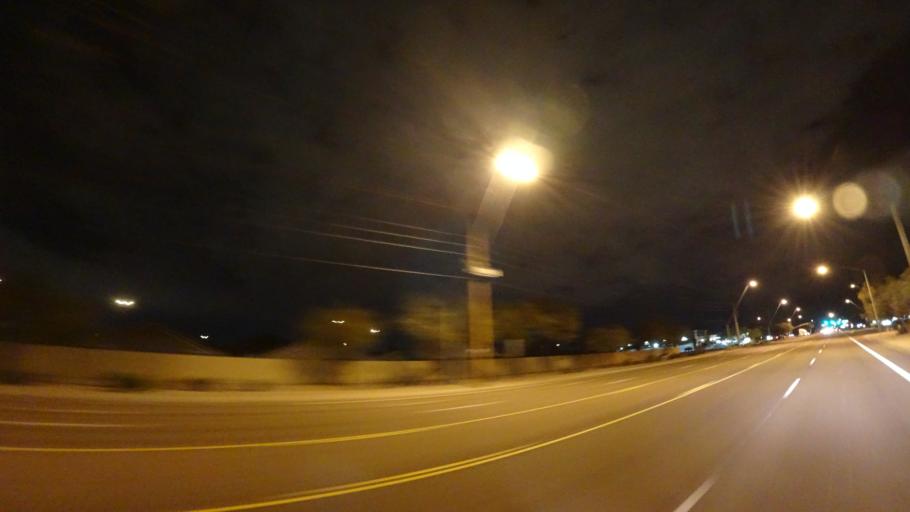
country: US
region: Arizona
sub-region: Maricopa County
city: San Carlos
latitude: 33.3642
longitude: -111.8450
